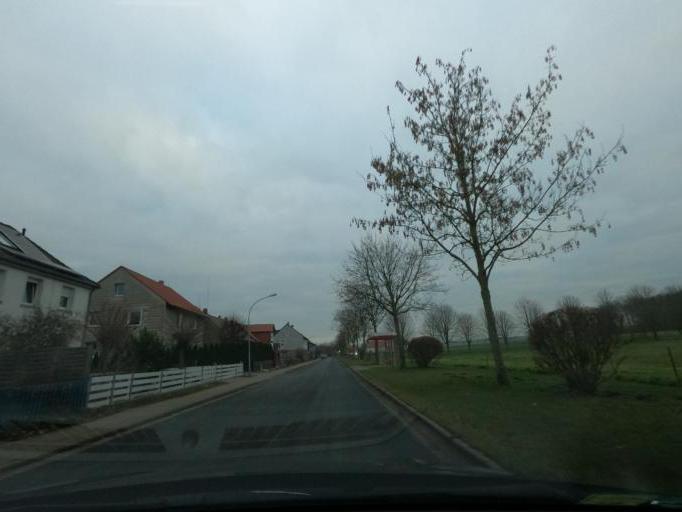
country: DE
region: Lower Saxony
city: Kissenbruck
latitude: 52.1096
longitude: 10.5827
